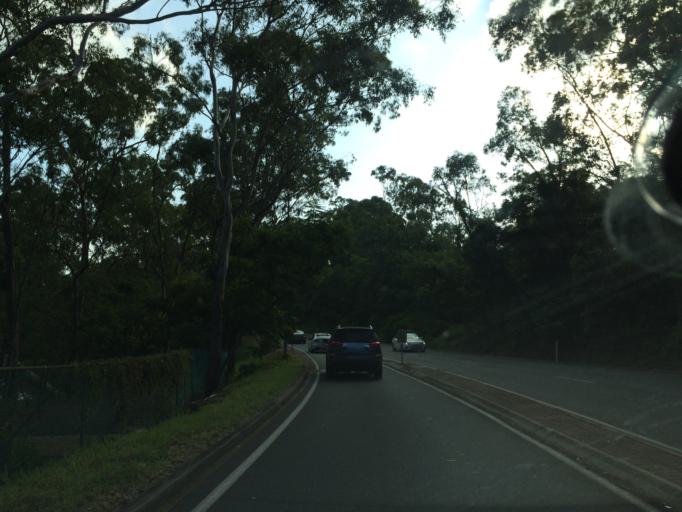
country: AU
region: Queensland
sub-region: Brisbane
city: Kenmore Hills
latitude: -27.5106
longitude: 152.9360
